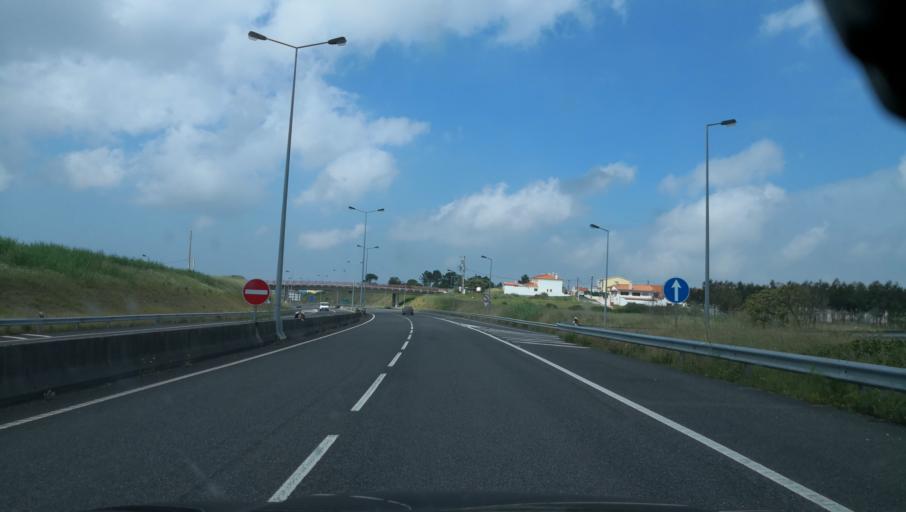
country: PT
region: Leiria
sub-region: Peniche
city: Atouguia da Baleia
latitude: 39.3312
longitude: -9.2578
